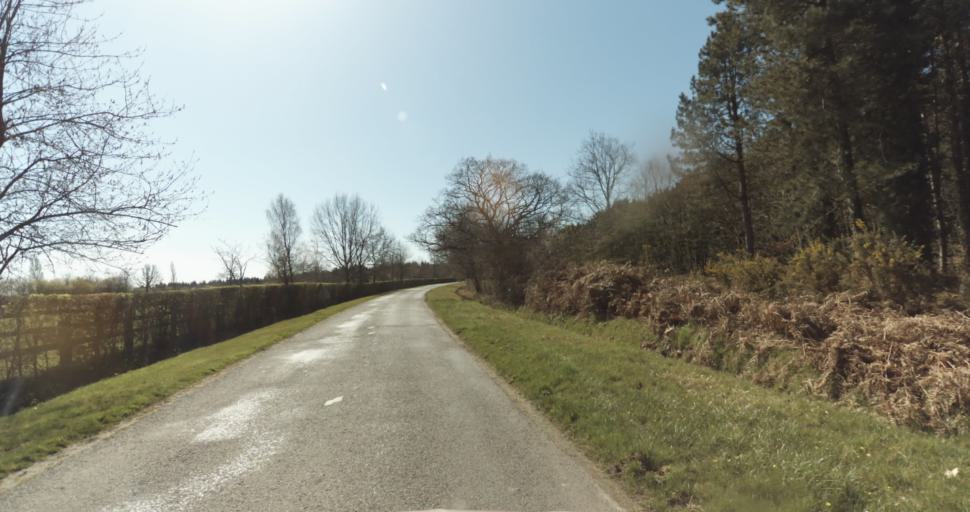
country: FR
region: Lower Normandy
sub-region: Departement du Calvados
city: Livarot
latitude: 48.9579
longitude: 0.0918
